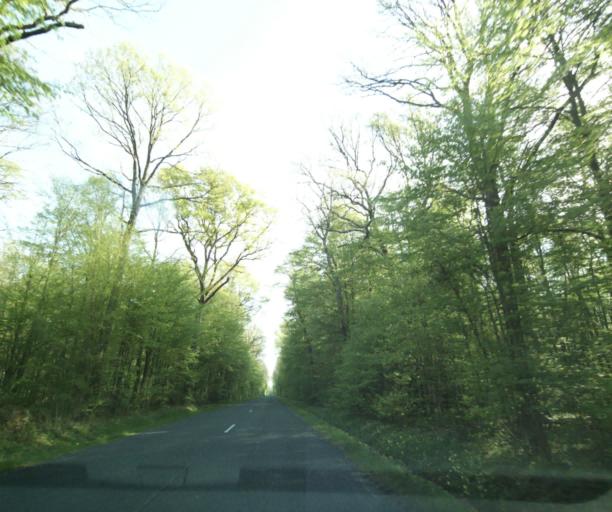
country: FR
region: Ile-de-France
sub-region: Departement de Seine-et-Marne
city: La Chapelle-Gauthier
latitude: 48.5067
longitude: 2.9211
